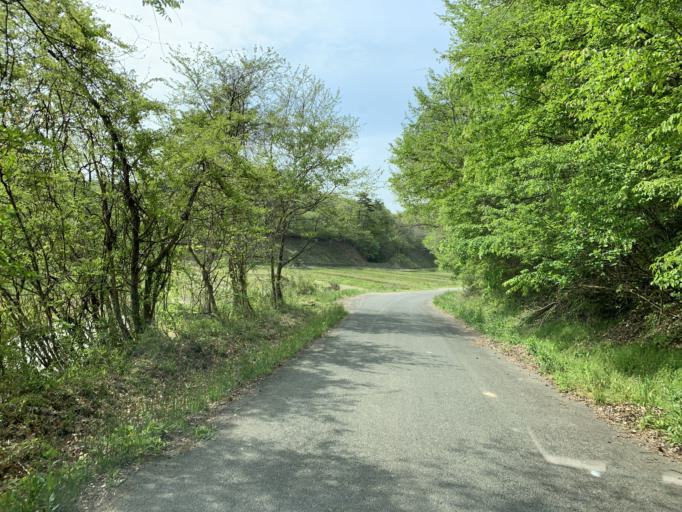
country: JP
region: Iwate
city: Ichinoseki
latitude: 38.8881
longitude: 141.0591
